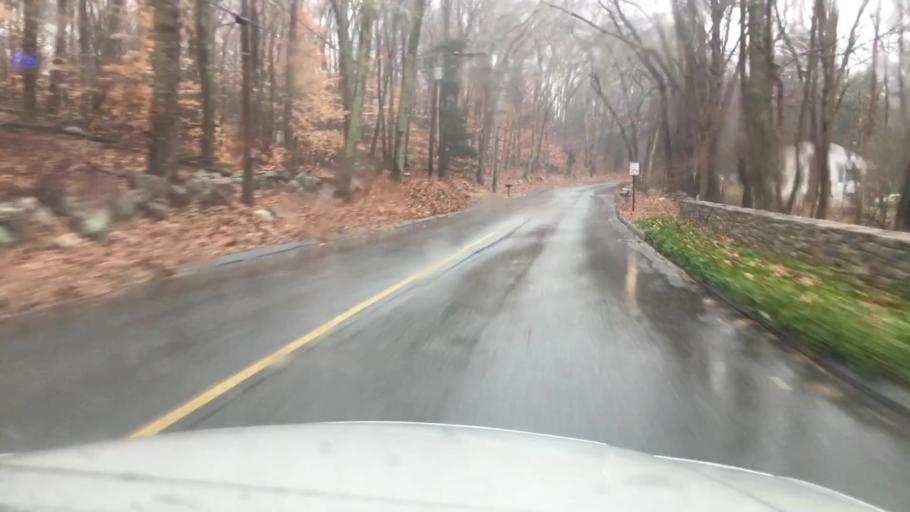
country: US
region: Connecticut
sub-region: Middlesex County
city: Essex Village
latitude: 41.3686
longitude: -72.4023
